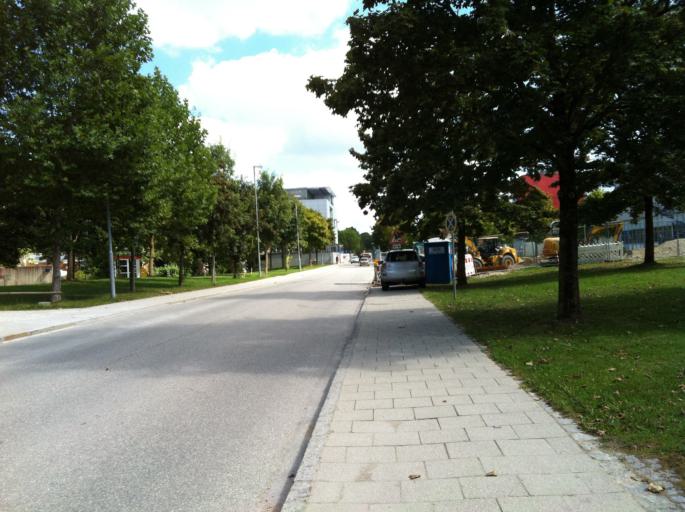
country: DE
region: Bavaria
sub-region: Upper Bavaria
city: Garching bei Munchen
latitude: 48.2670
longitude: 11.6696
